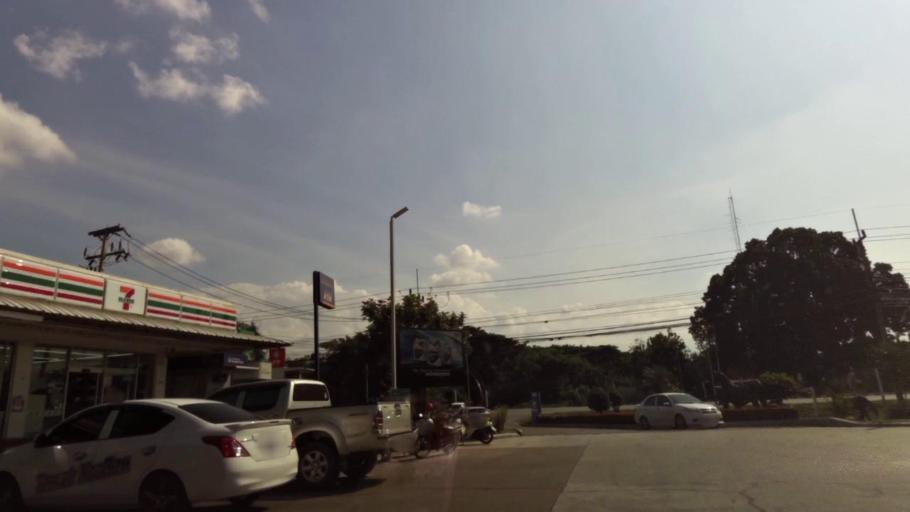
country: TH
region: Phrae
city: Phrae
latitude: 18.1348
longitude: 100.1269
